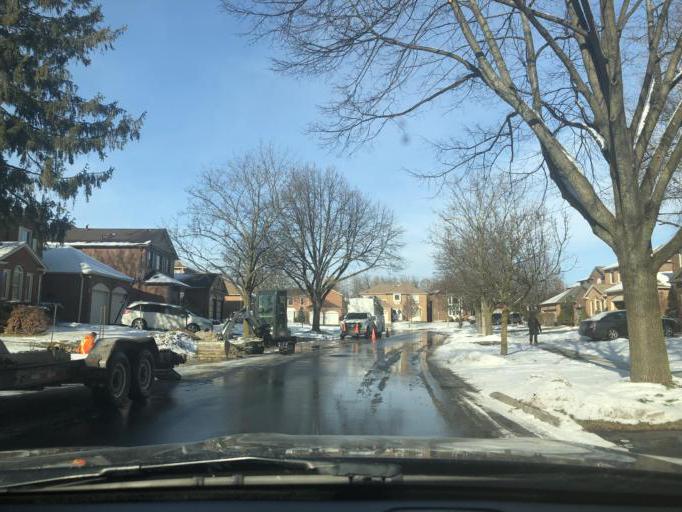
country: CA
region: Ontario
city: Scarborough
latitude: 43.7855
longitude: -79.1514
